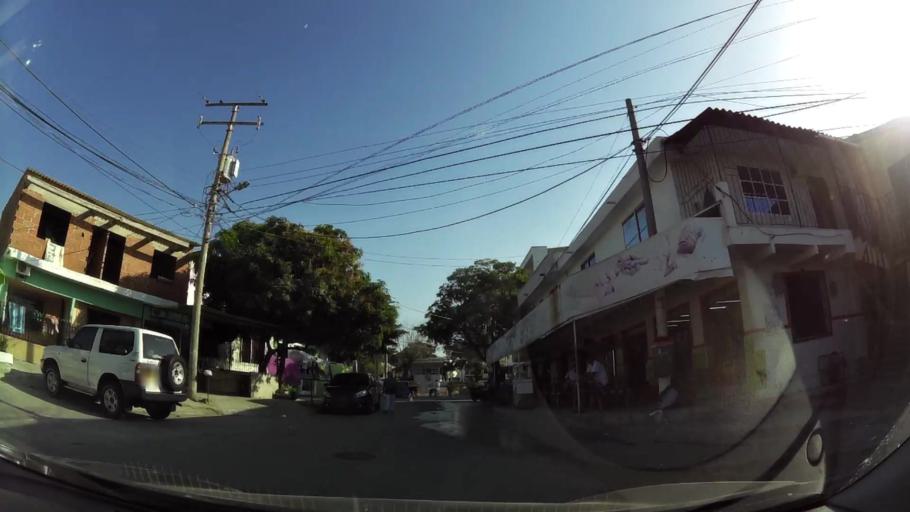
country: CO
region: Bolivar
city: Cartagena
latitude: 10.3850
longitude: -75.4806
